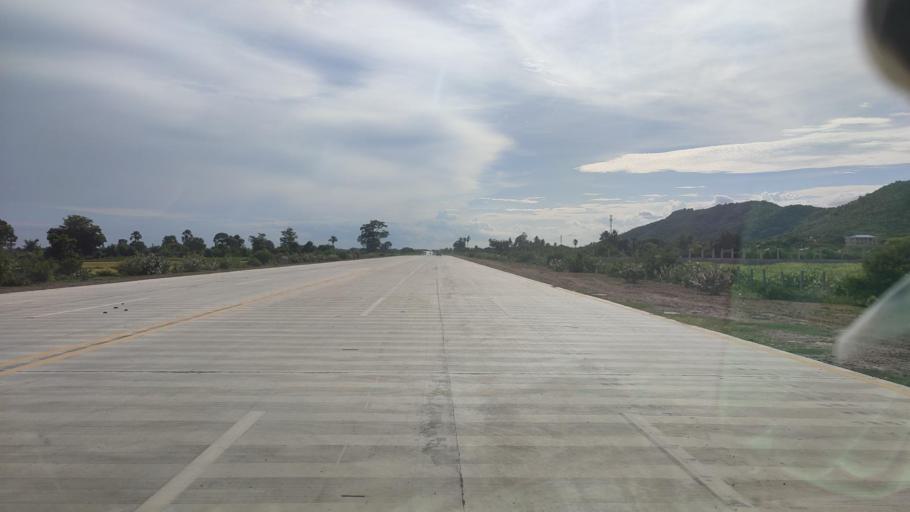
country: MM
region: Mandalay
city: Kyaukse
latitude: 21.5994
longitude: 96.1768
